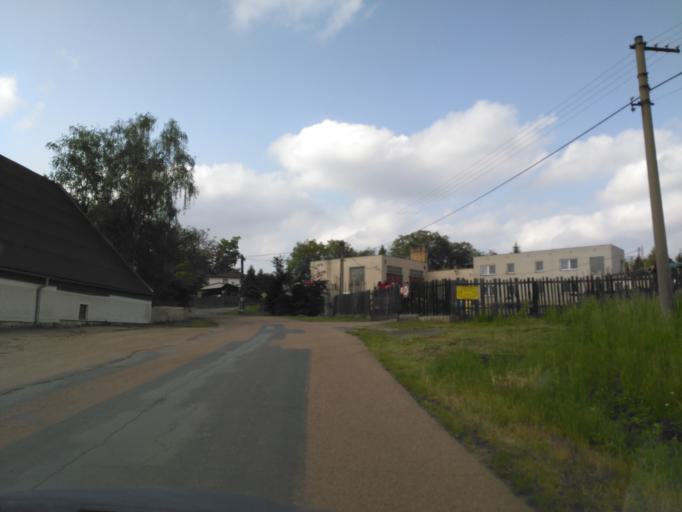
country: CZ
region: Plzensky
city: Zbiroh
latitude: 49.8557
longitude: 13.7527
